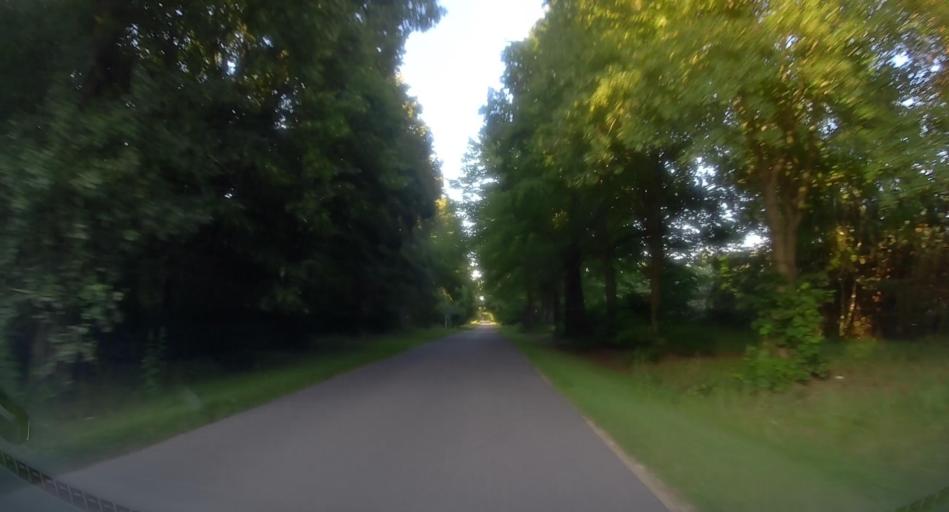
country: PL
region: Lodz Voivodeship
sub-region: Powiat skierniewicki
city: Kaweczyn Nowy
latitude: 51.9034
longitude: 20.3145
